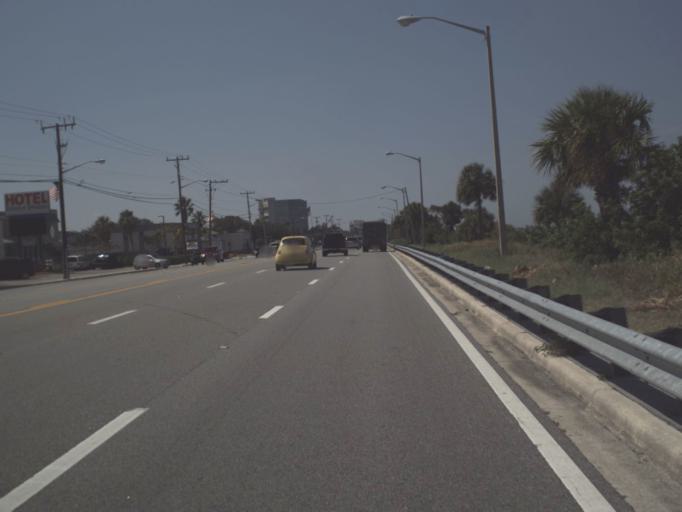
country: US
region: Florida
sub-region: Brevard County
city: Melbourne
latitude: 28.1026
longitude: -80.6143
